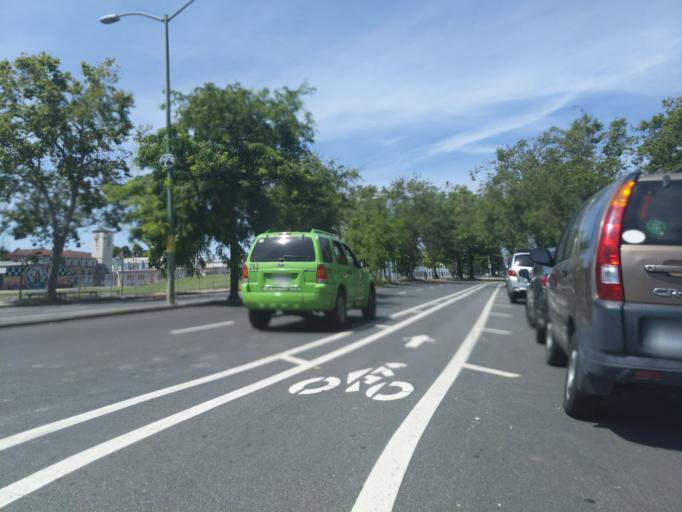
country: US
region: California
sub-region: Alameda County
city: Oakland
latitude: 37.8056
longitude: -122.2818
